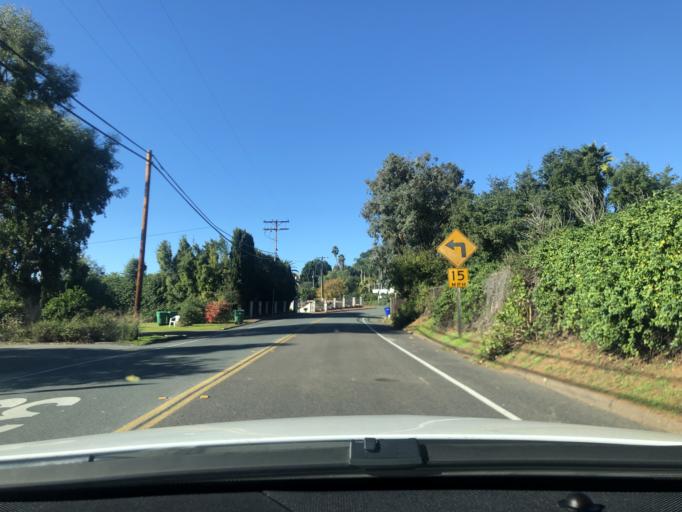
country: US
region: California
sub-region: San Diego County
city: Rancho San Diego
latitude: 32.7693
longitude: -116.9394
